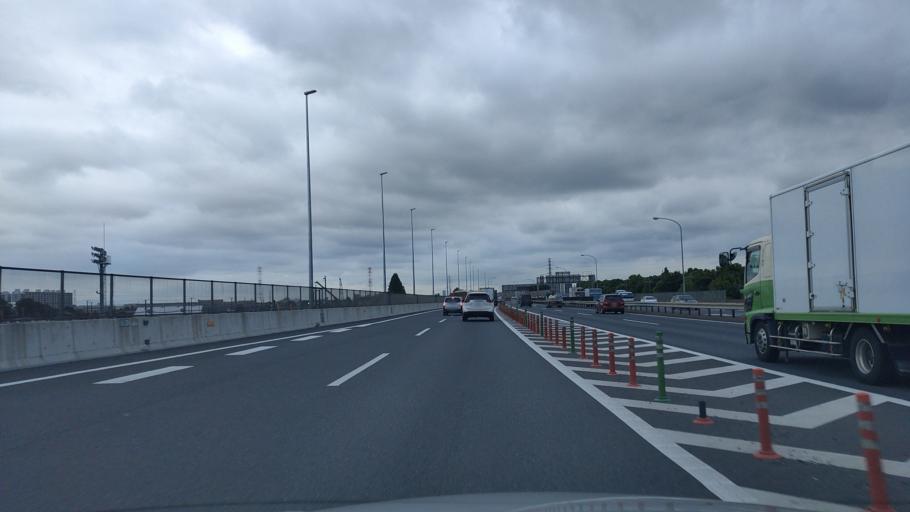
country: JP
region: Saitama
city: Yashio-shi
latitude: 35.8392
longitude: 139.8649
